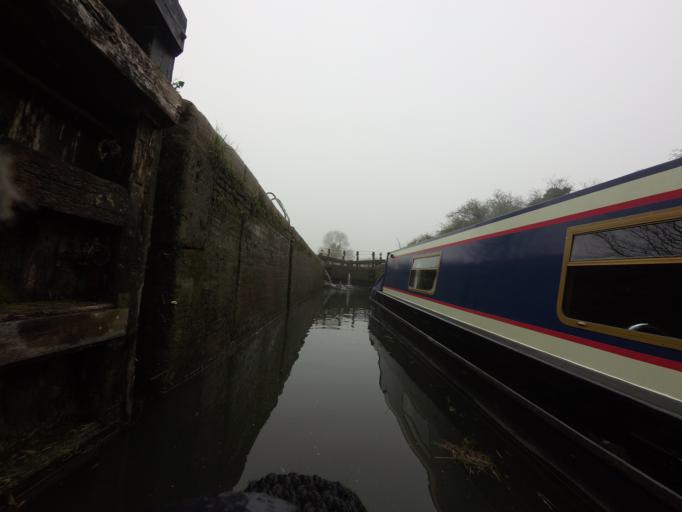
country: GB
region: England
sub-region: Hertfordshire
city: Tring
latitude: 51.8168
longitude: -0.6640
